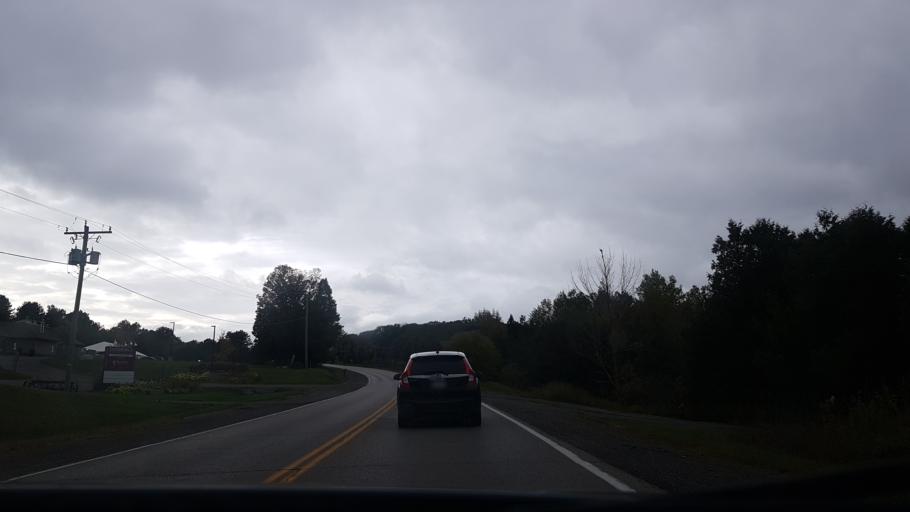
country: CA
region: Ontario
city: Uxbridge
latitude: 44.1041
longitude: -79.0920
